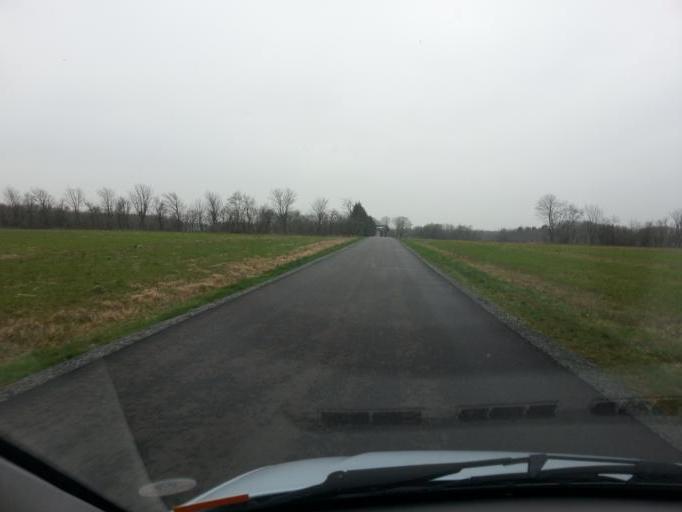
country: DK
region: South Denmark
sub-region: Varde Kommune
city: Varde
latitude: 55.5690
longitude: 8.5181
